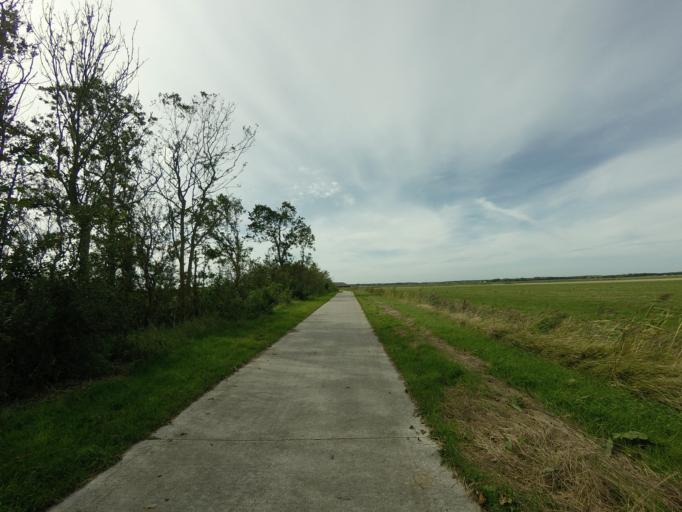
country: NL
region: North Holland
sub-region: Gemeente Texel
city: Den Burg
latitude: 53.0743
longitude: 4.8064
